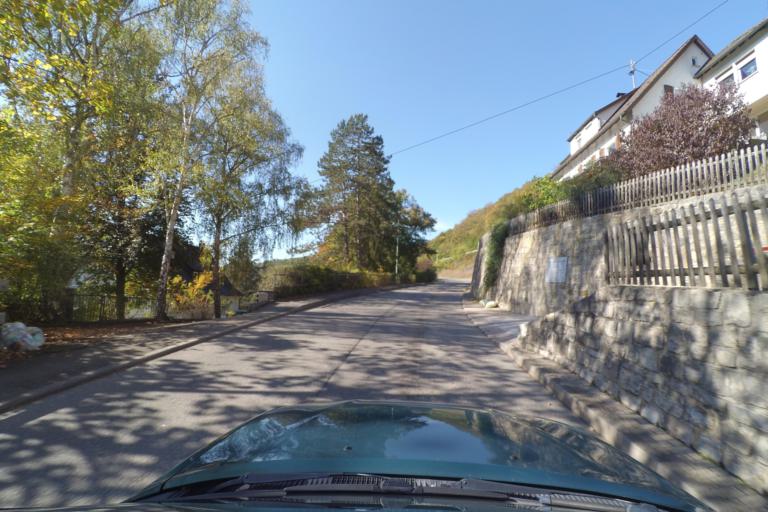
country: DE
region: Baden-Wuerttemberg
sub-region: Karlsruhe Region
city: Horb am Neckar
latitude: 48.4514
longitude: 8.7299
